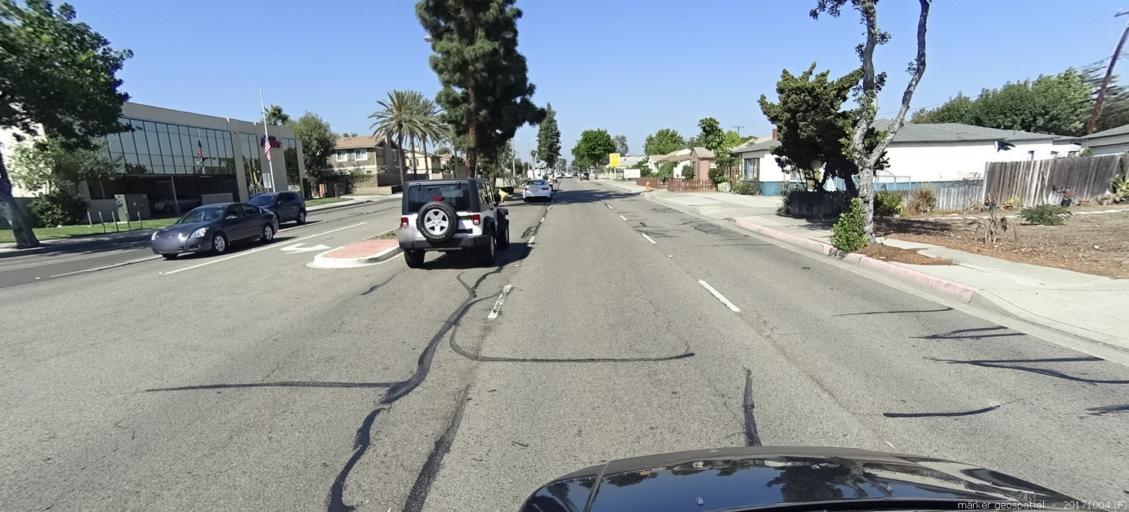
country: US
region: California
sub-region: Orange County
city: Garden Grove
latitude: 33.7832
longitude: -117.9410
